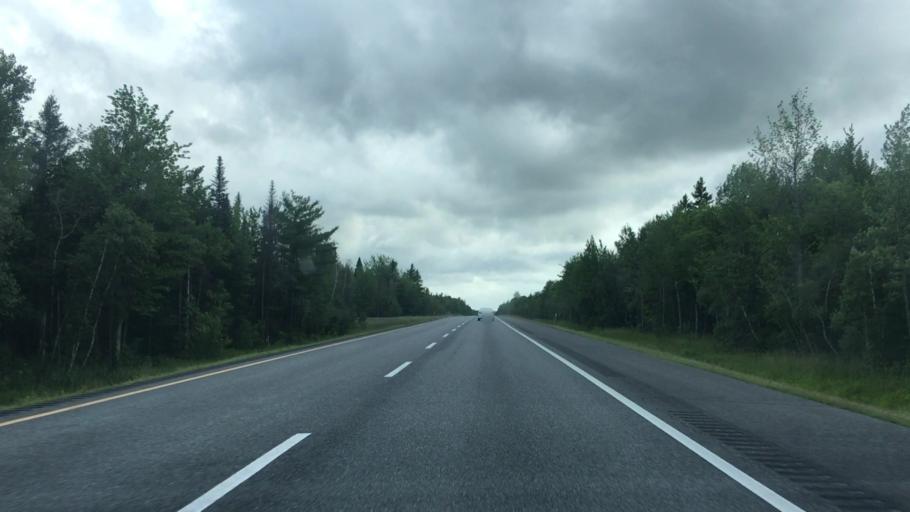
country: US
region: Maine
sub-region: Kennebec County
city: Clinton
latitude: 44.6815
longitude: -69.4789
